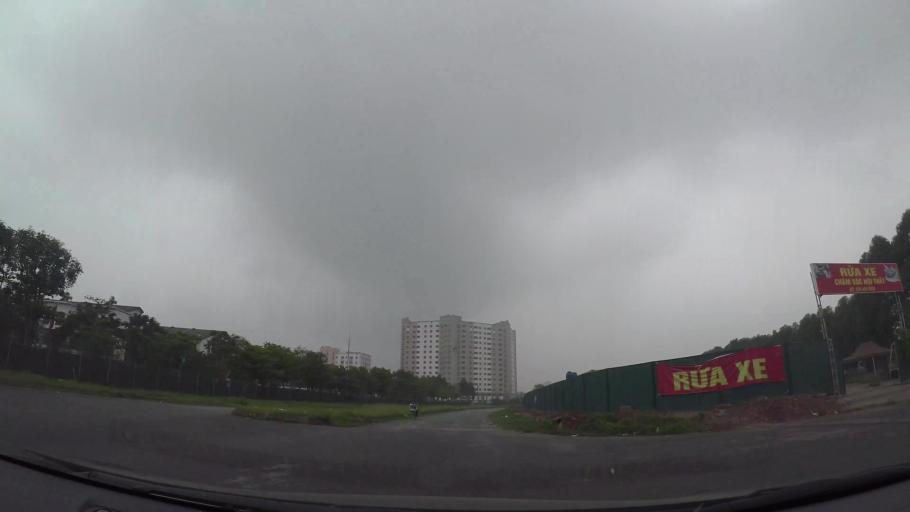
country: VN
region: Ha Noi
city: Van Dien
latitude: 20.9746
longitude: 105.8781
